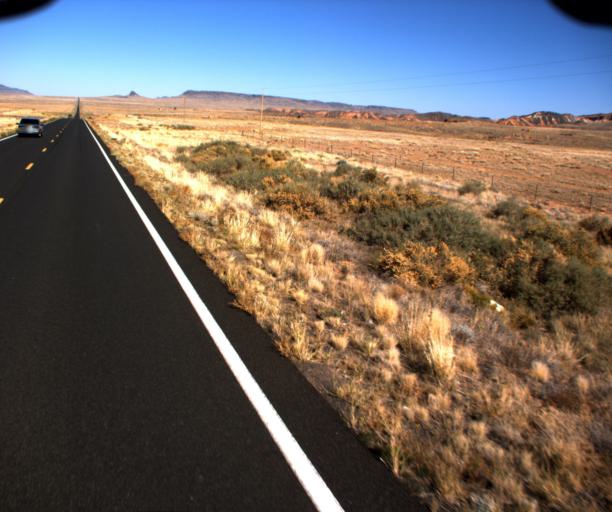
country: US
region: Arizona
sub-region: Navajo County
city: Dilkon
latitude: 35.3172
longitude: -110.4230
